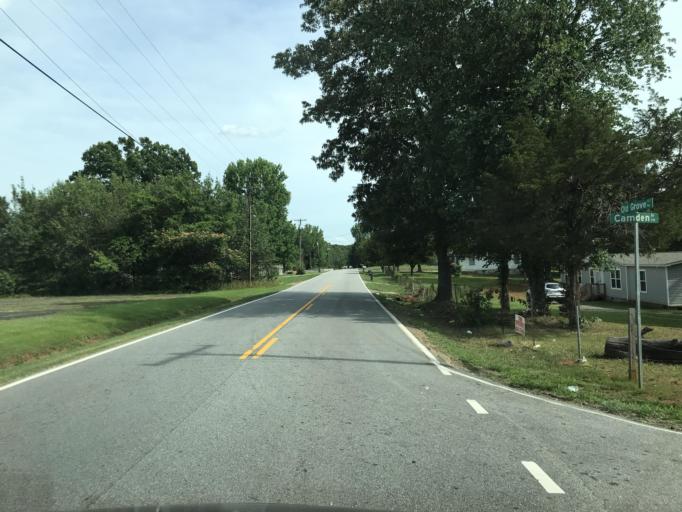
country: US
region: South Carolina
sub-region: Greenville County
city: Gantt
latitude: 34.7667
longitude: -82.4153
